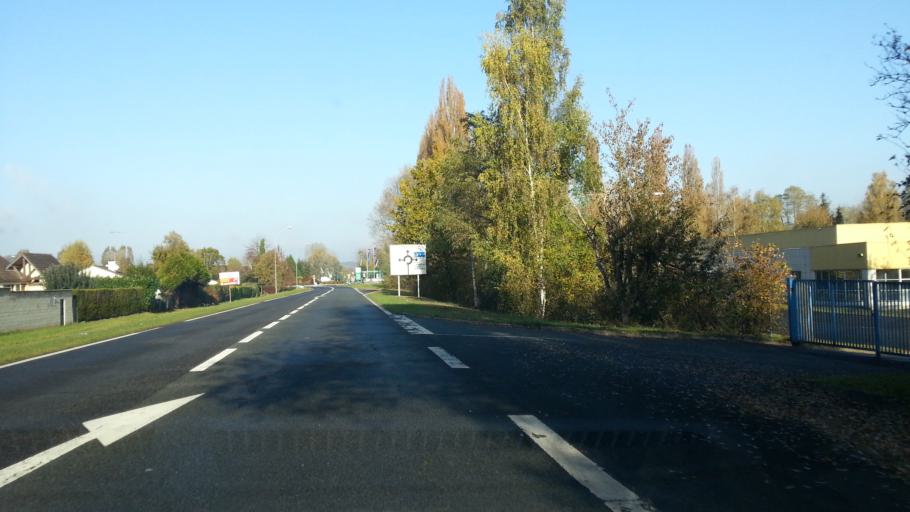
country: FR
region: Picardie
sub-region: Departement de l'Oise
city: Mouy
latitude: 49.3081
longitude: 2.3279
